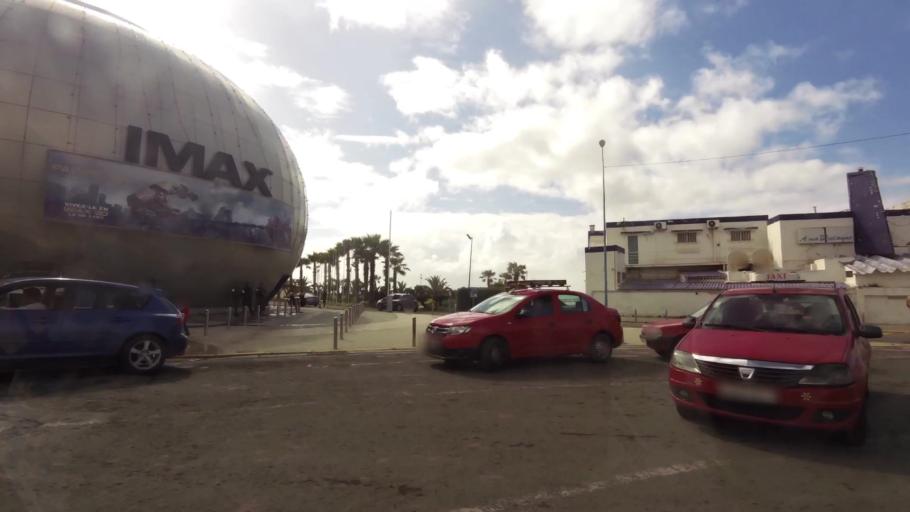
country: MA
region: Grand Casablanca
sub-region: Casablanca
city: Casablanca
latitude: 33.5776
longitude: -7.7045
